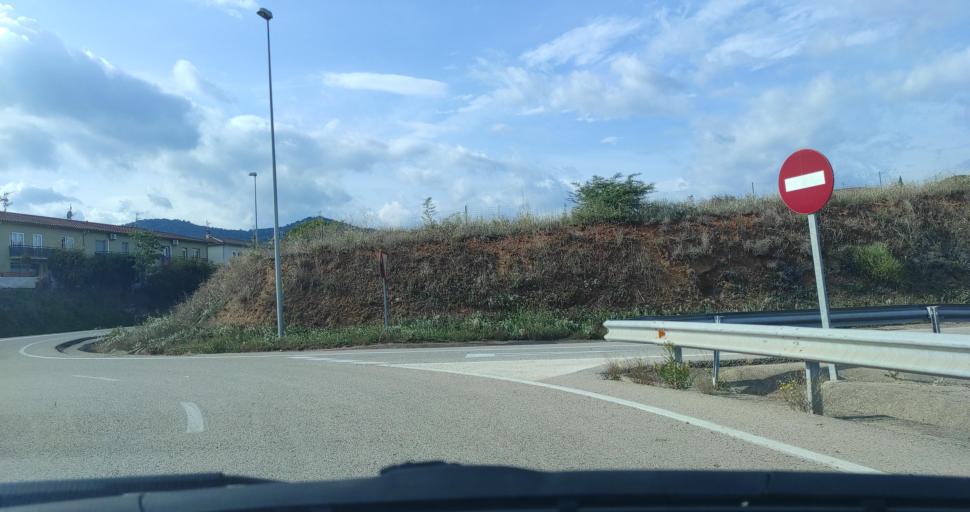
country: ES
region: Catalonia
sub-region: Provincia de Girona
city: Besalu
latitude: 42.2035
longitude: 2.7056
